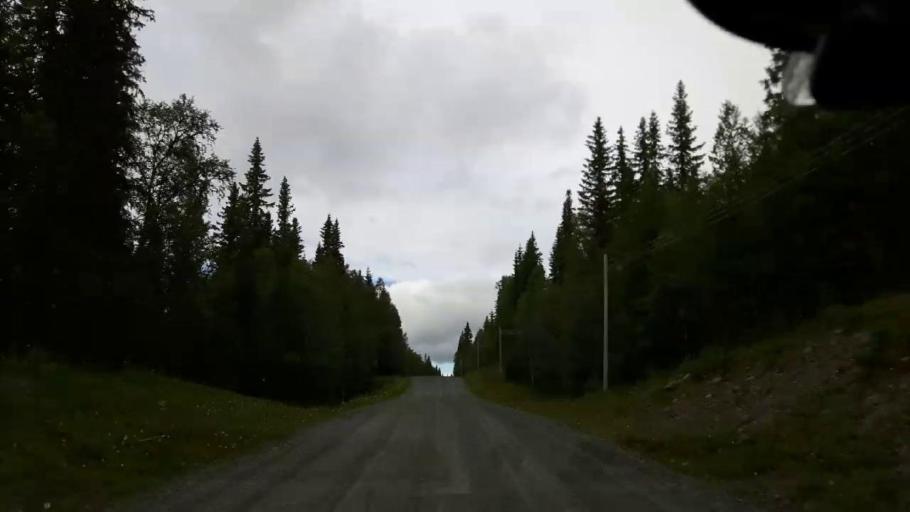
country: SE
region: Jaemtland
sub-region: Krokoms Kommun
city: Valla
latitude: 63.7210
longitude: 13.8539
